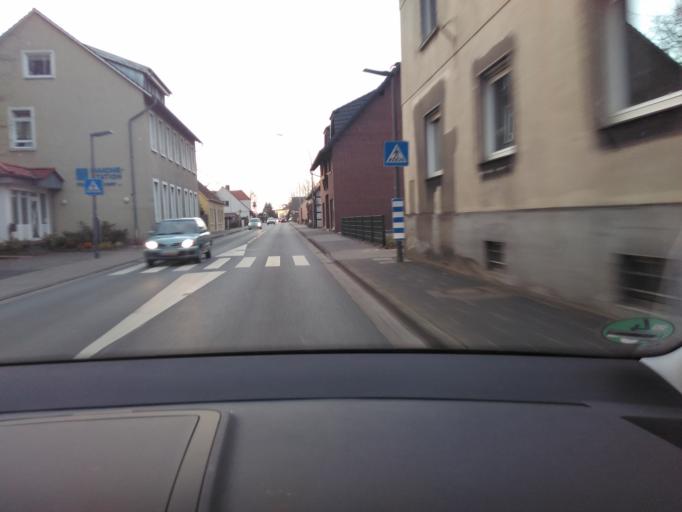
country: DE
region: North Rhine-Westphalia
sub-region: Regierungsbezirk Detmold
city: Verl
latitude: 51.9377
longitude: 8.4874
